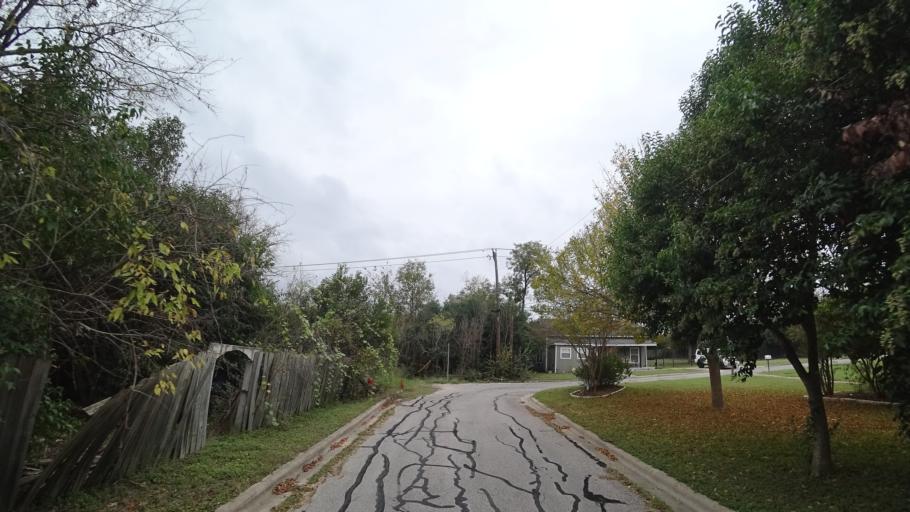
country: US
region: Texas
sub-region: Travis County
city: Pflugerville
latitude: 30.4359
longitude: -97.6162
